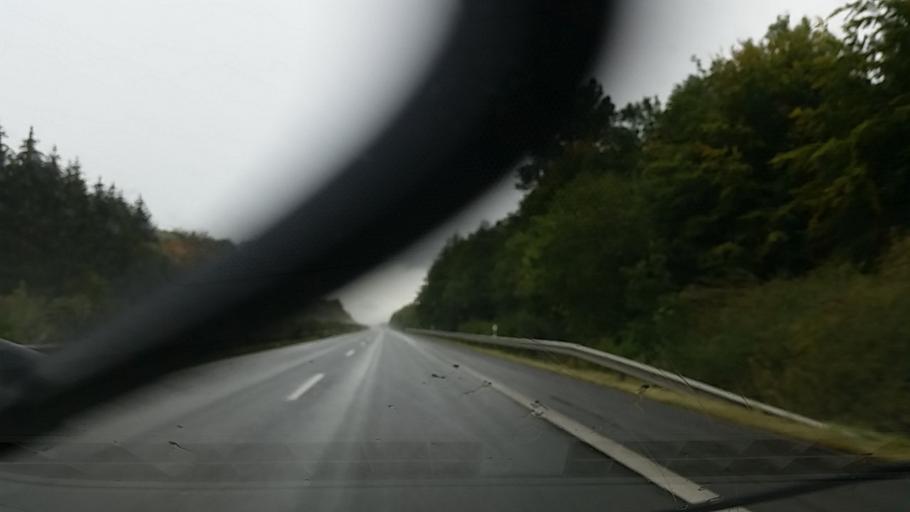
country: DE
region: Lower Saxony
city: Flothe
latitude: 52.1054
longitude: 10.4898
